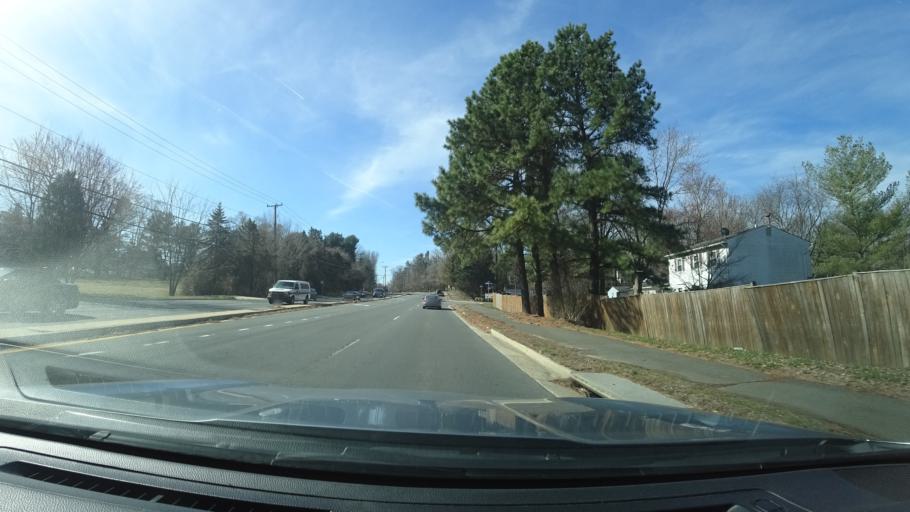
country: US
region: Virginia
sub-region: Fairfax County
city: Oak Hill
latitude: 38.9152
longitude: -77.3783
